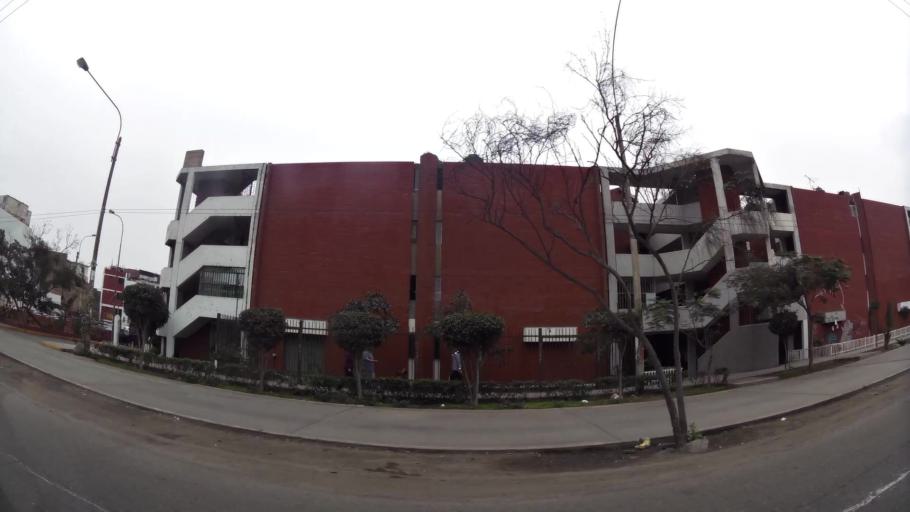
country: PE
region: Lima
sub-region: Lima
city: San Luis
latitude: -12.0794
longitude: -77.0123
